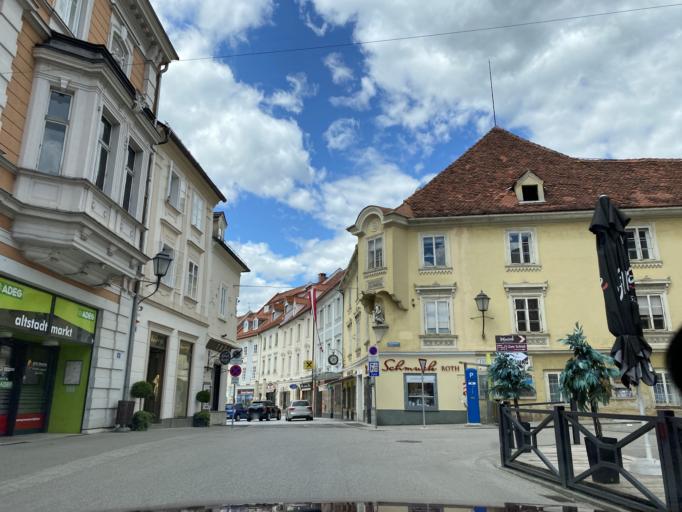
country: AT
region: Carinthia
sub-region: Politischer Bezirk Wolfsberg
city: Wolfsberg
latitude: 46.8388
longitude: 14.8456
